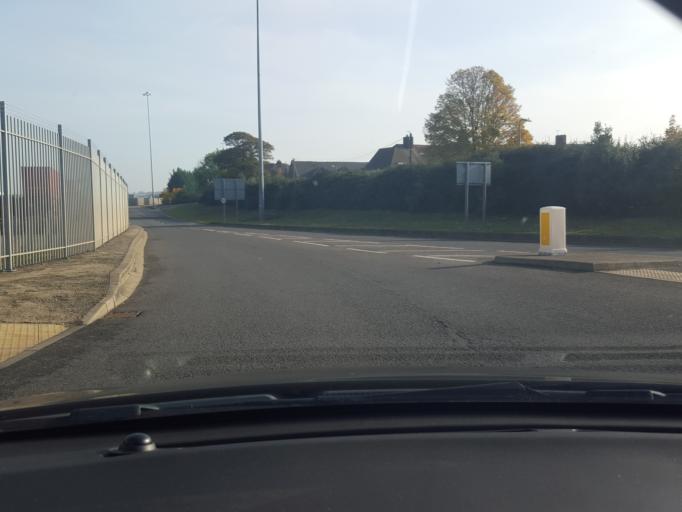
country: GB
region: England
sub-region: Suffolk
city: Shotley Gate
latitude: 51.9452
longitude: 1.2521
